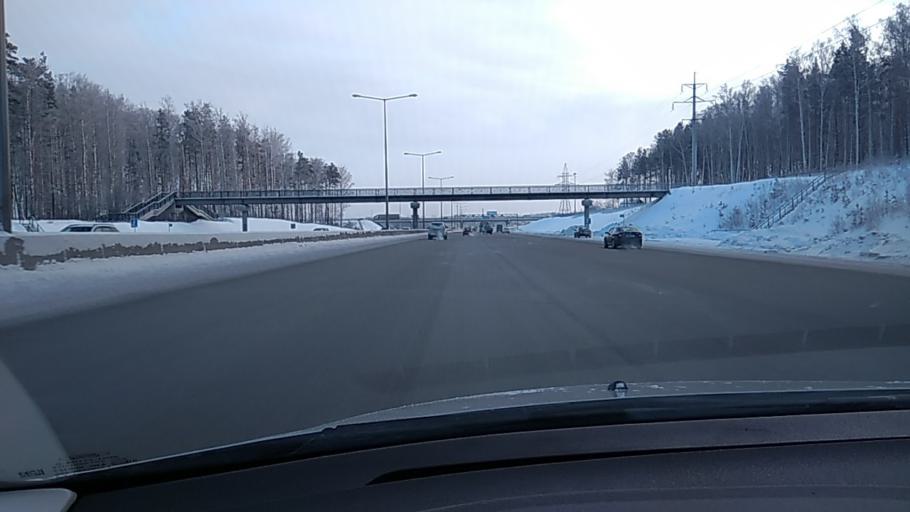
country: RU
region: Sverdlovsk
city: Istok
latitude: 56.7702
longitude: 60.7302
